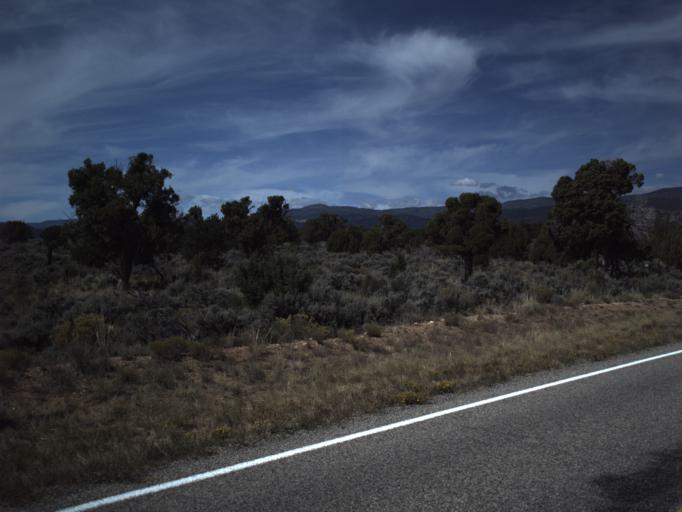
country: US
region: Utah
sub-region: Wayne County
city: Loa
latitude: 37.8810
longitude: -111.4574
